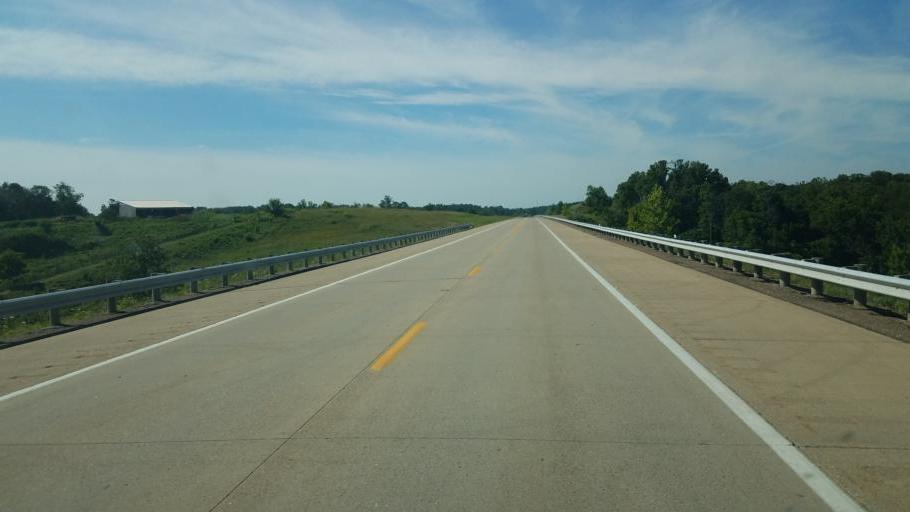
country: US
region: Ohio
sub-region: Athens County
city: Athens
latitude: 39.1860
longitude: -82.0500
